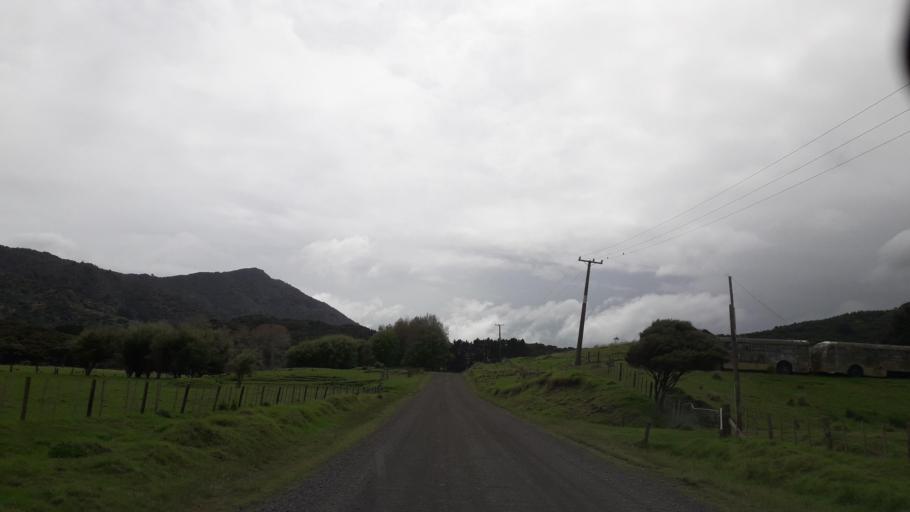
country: NZ
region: Northland
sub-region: Far North District
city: Ahipara
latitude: -35.4402
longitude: 173.3265
